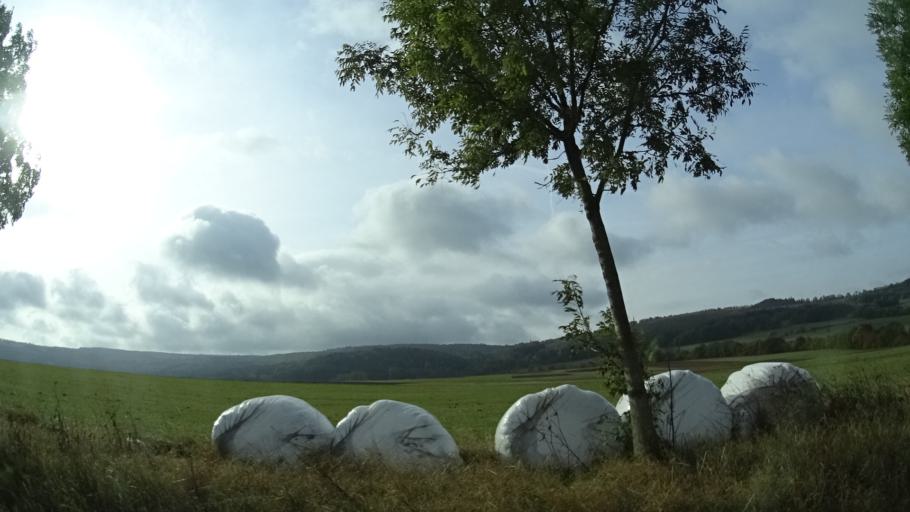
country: DE
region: Thuringia
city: Oberweid
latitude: 50.5910
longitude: 10.0416
